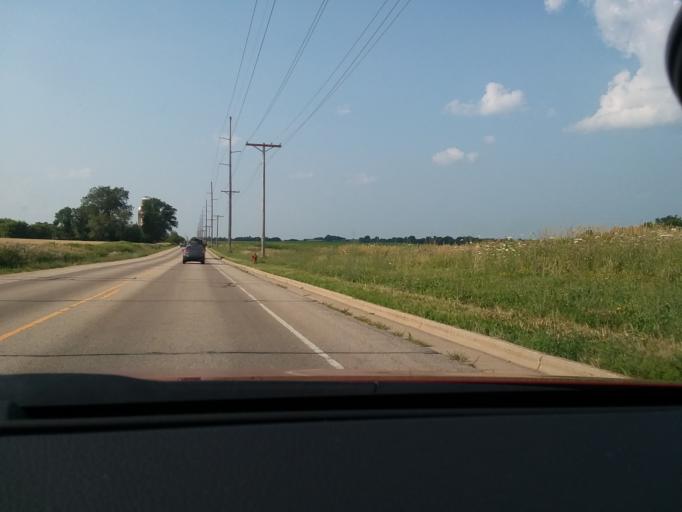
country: US
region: Wisconsin
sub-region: Dane County
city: Cottage Grove
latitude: 43.1098
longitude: -89.2666
